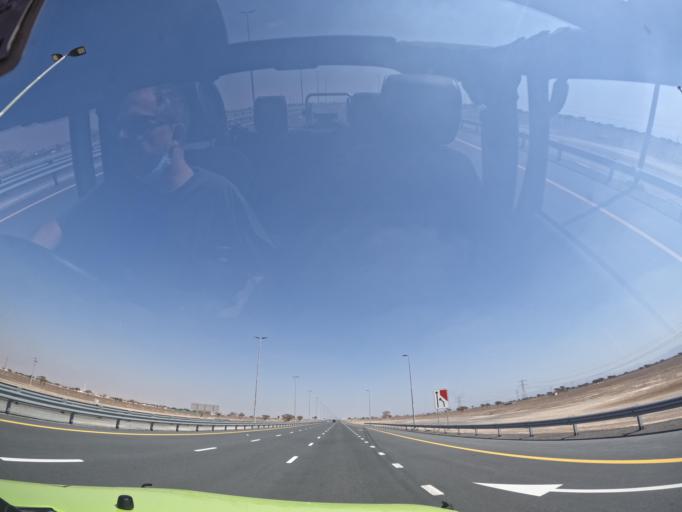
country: AE
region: Ash Shariqah
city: Adh Dhayd
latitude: 24.9593
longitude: 55.8406
